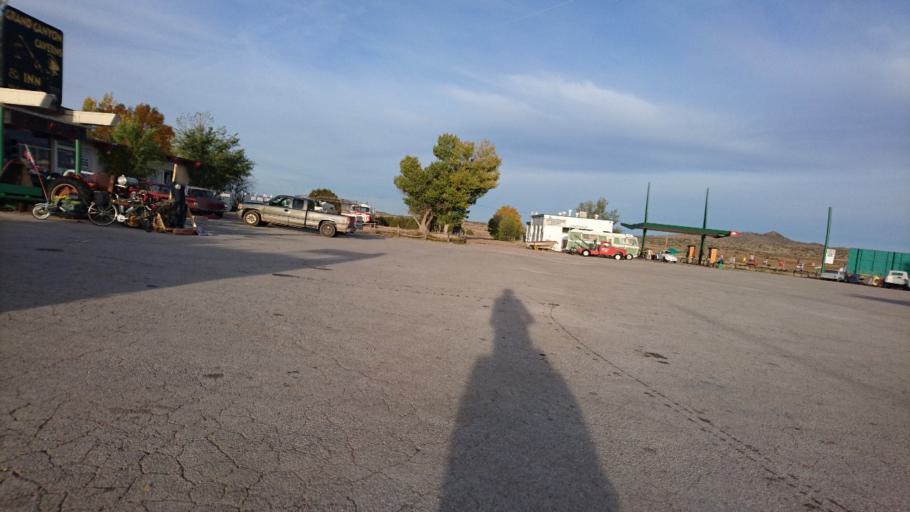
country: US
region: Arizona
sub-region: Mohave County
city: Peach Springs
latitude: 35.5289
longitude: -113.2308
